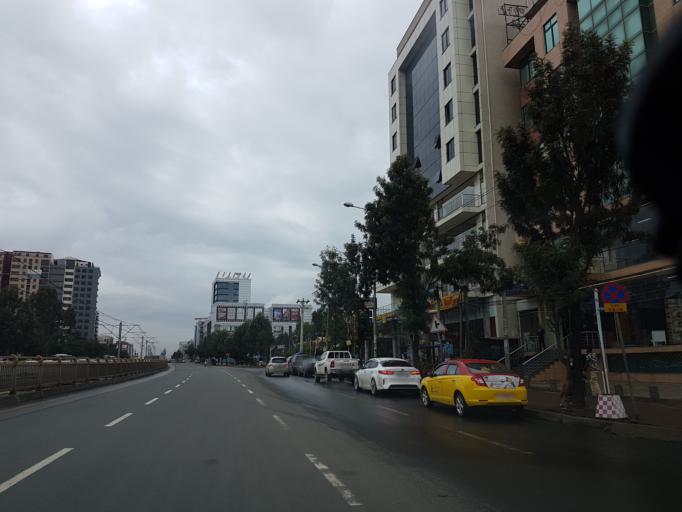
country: ET
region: Adis Abeba
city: Addis Ababa
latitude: 9.0200
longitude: 38.8109
